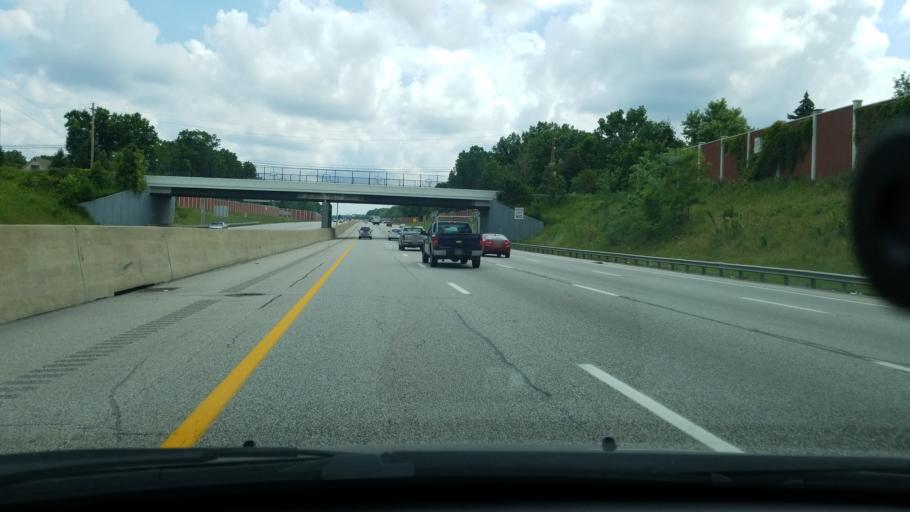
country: US
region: Ohio
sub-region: Cuyahoga County
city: Independence
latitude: 41.3860
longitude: -81.6529
